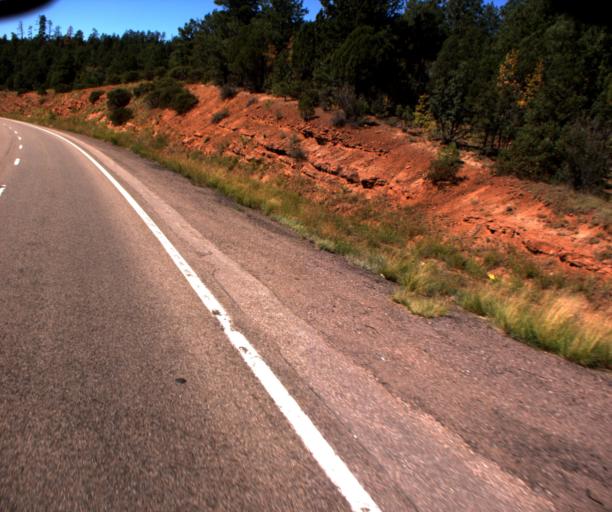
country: US
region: Arizona
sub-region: Gila County
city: Star Valley
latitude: 34.3062
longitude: -110.9506
